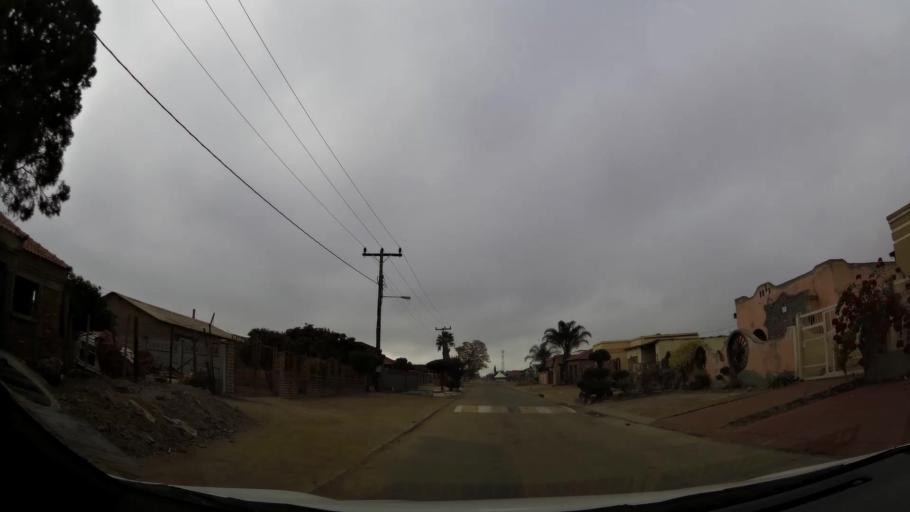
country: ZA
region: Limpopo
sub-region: Capricorn District Municipality
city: Polokwane
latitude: -23.8358
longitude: 29.3893
